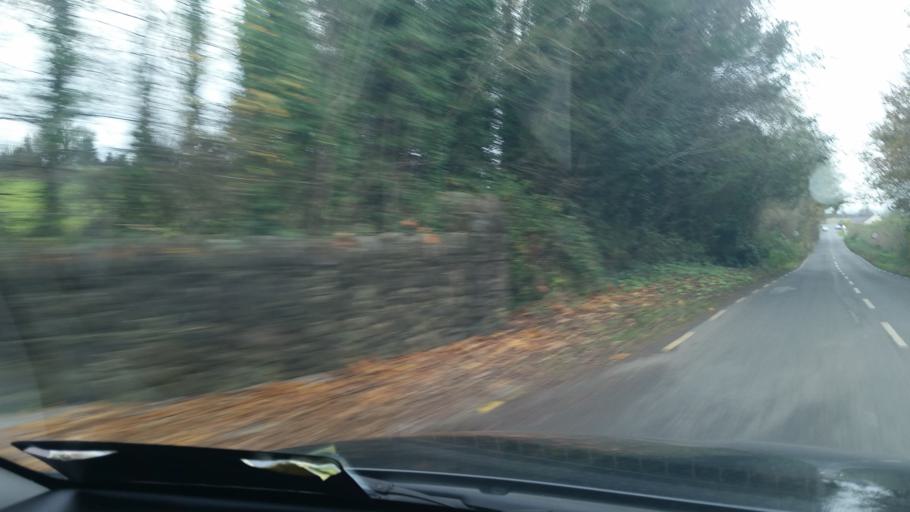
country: IE
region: Leinster
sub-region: An Mhi
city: Duleek
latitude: 53.6952
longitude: -6.4116
